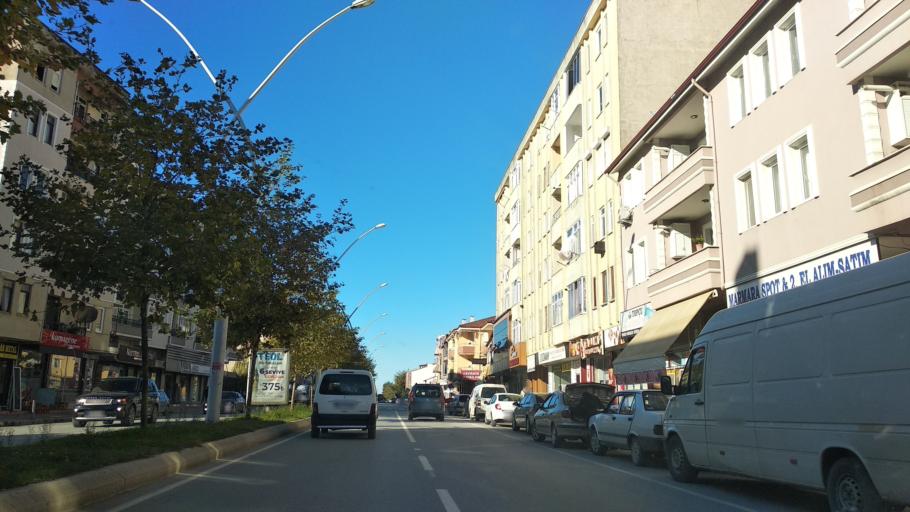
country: TR
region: Sakarya
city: Karasu
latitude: 41.1014
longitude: 30.6926
